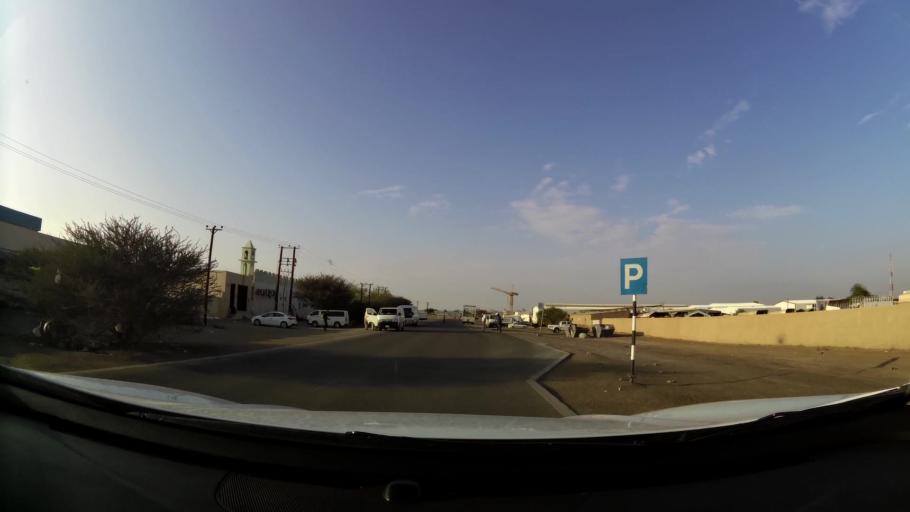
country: AE
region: Abu Dhabi
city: Al Ain
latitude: 24.1482
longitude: 55.8257
